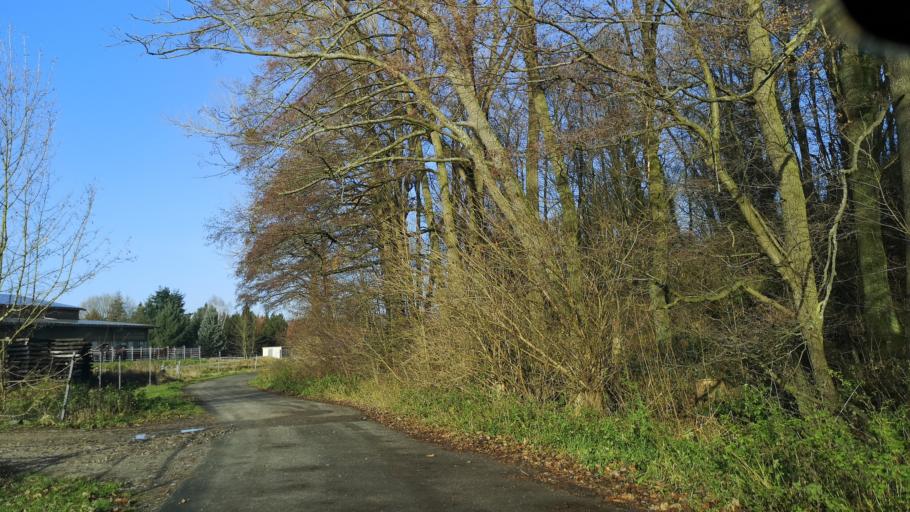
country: DE
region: Hesse
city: Ober-Ramstadt
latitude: 49.7846
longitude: 8.7448
